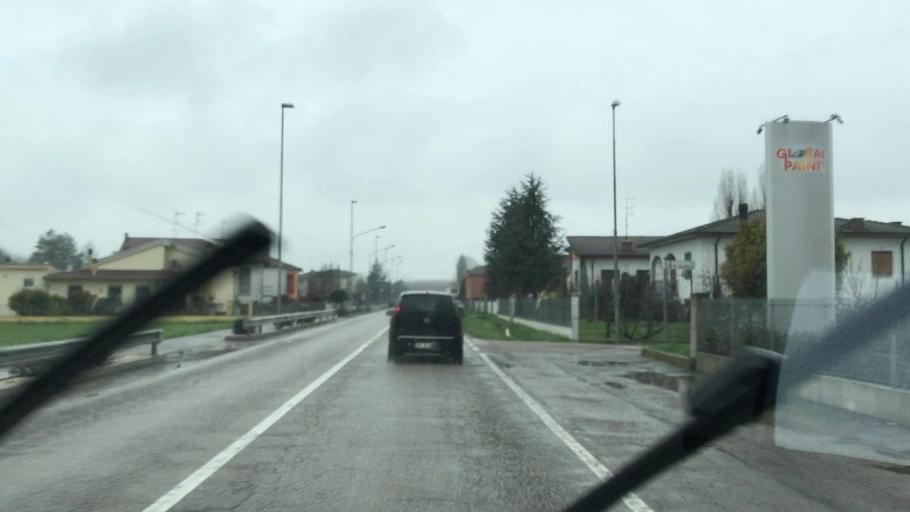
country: IT
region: Lombardy
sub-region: Provincia di Mantova
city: Borgofranco sul Po
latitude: 45.0474
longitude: 11.2079
